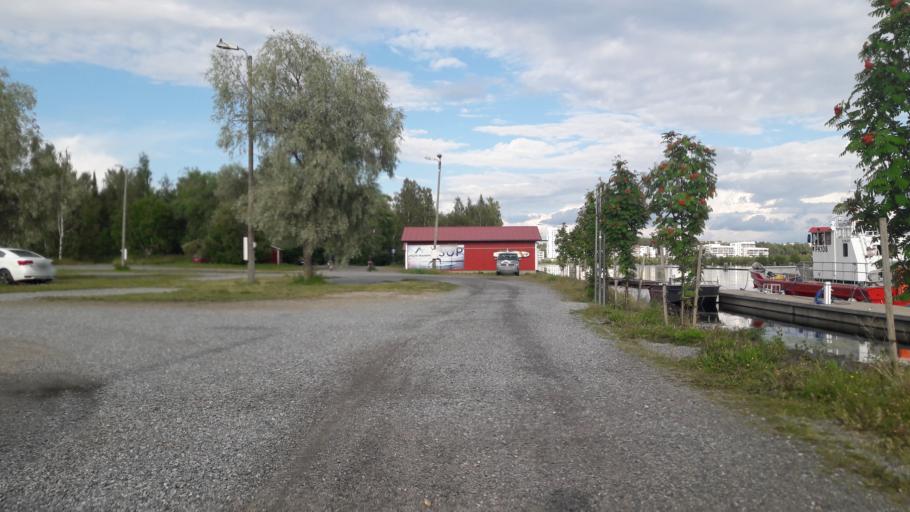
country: FI
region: North Karelia
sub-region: Joensuu
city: Joensuu
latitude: 62.5909
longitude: 29.7403
